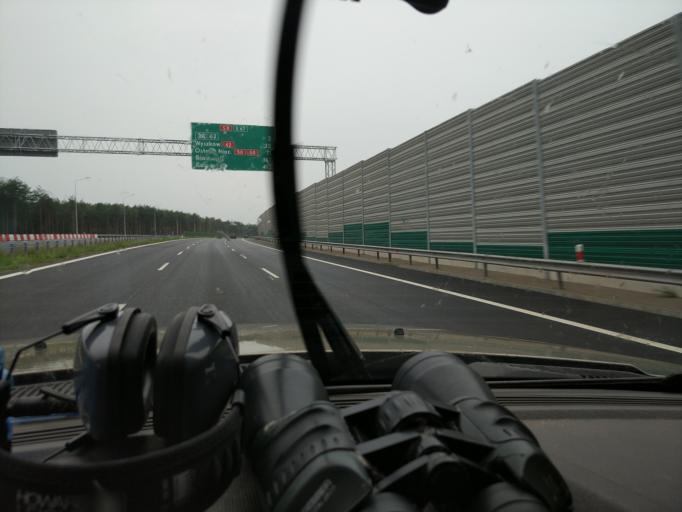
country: PL
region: Masovian Voivodeship
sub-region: Powiat wolominski
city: Slupno
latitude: 52.3754
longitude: 21.1882
